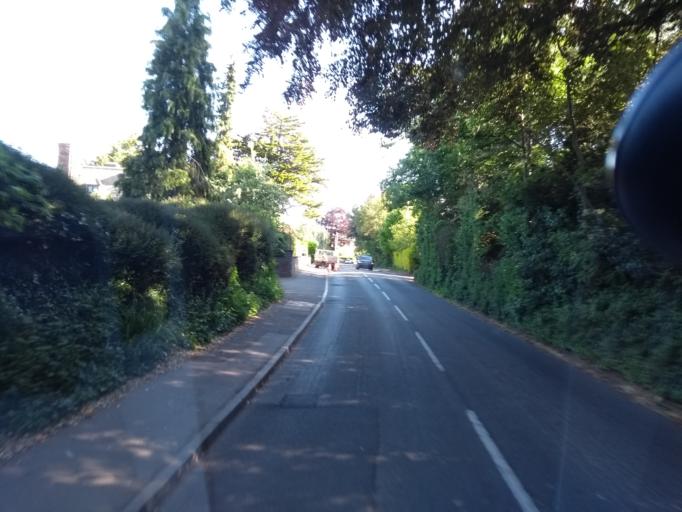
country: GB
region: England
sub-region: Somerset
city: Taunton
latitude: 51.0053
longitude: -3.1130
